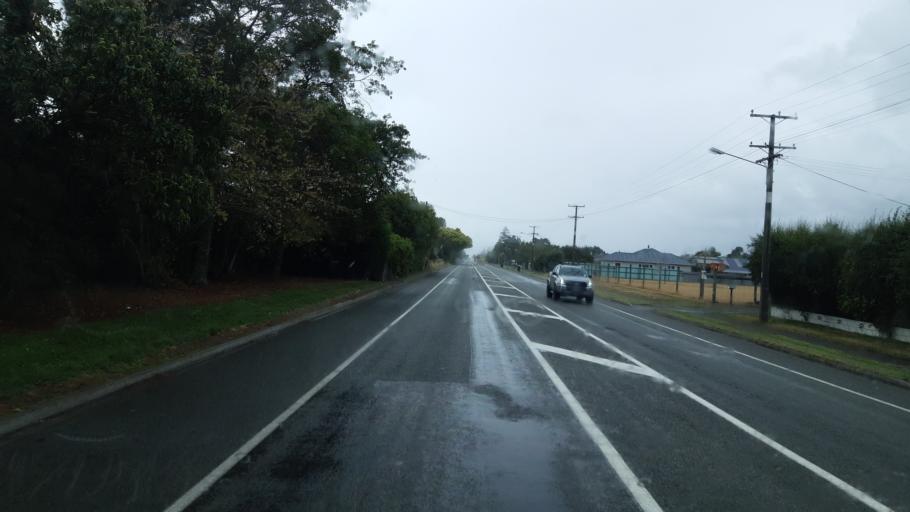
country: NZ
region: Tasman
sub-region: Tasman District
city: Brightwater
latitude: -41.3573
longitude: 173.1487
